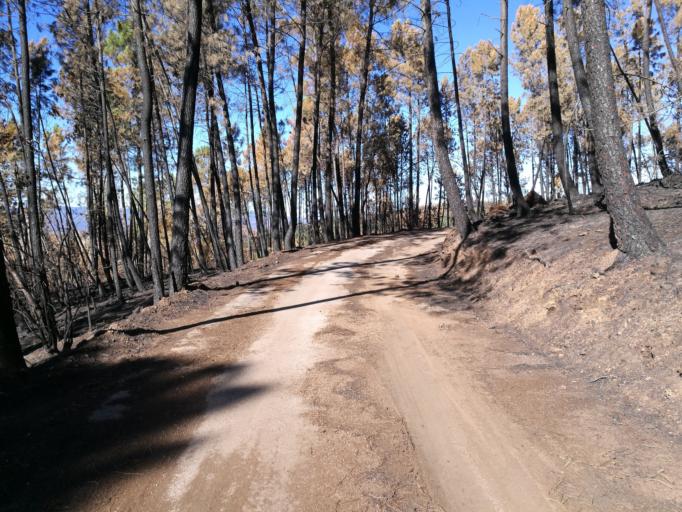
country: PT
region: Leiria
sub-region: Pedrogao Grande
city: Pedrogao Grande
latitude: 39.9121
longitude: -8.0671
